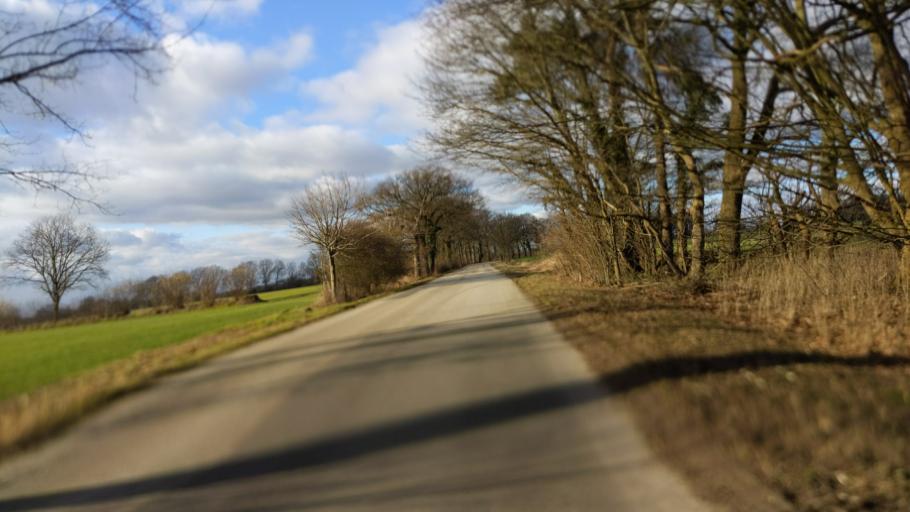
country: DE
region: Schleswig-Holstein
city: Susel
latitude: 54.0686
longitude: 10.7171
